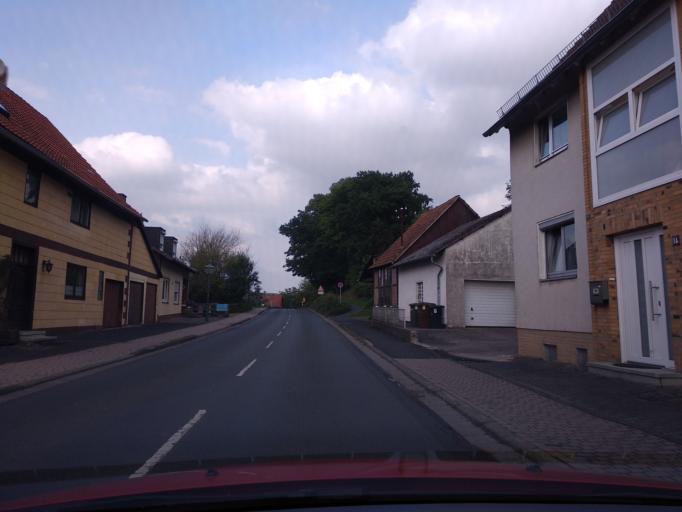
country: DE
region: Hesse
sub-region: Regierungsbezirk Kassel
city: Calden
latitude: 51.3666
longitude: 9.3949
